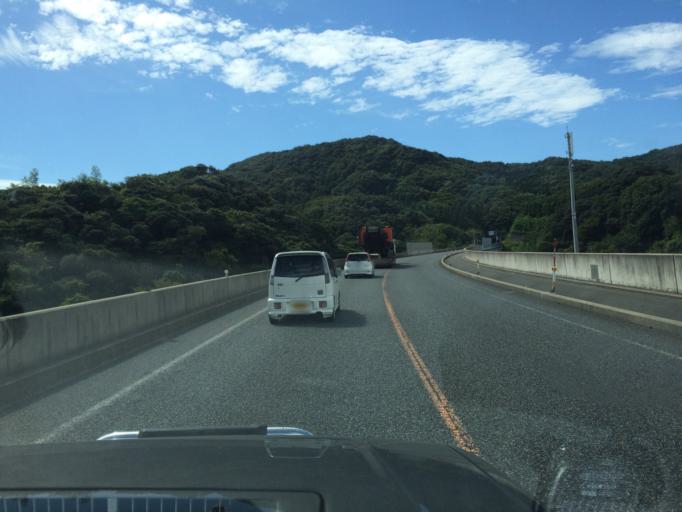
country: JP
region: Tottori
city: Tottori
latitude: 35.5163
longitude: 134.0238
